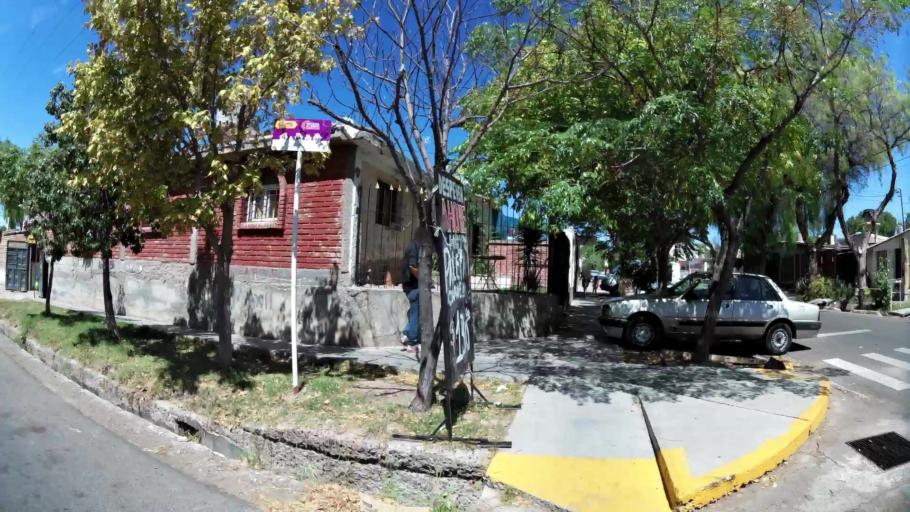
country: AR
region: Mendoza
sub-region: Departamento de Godoy Cruz
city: Godoy Cruz
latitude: -32.9458
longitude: -68.8684
